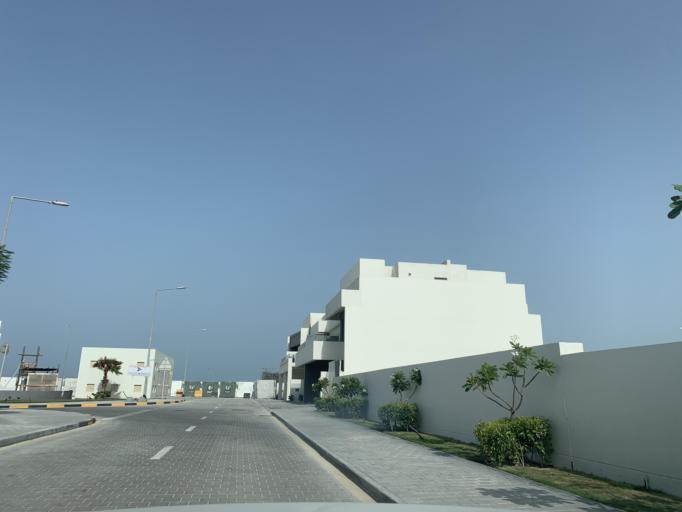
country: BH
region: Muharraq
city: Al Muharraq
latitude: 26.3101
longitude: 50.6363
